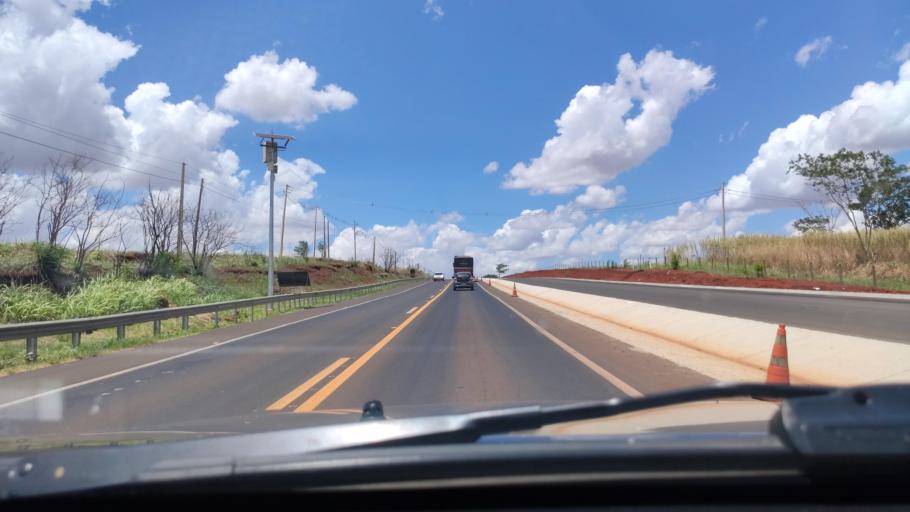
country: BR
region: Sao Paulo
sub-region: Jau
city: Jau
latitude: -22.2372
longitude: -48.5369
